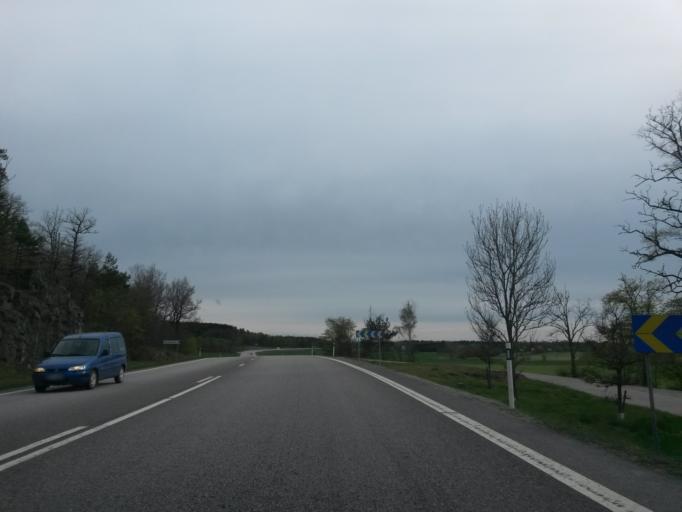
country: SE
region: Vaestra Goetaland
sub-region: Vargarda Kommun
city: Vargarda
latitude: 58.1108
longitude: 12.8411
